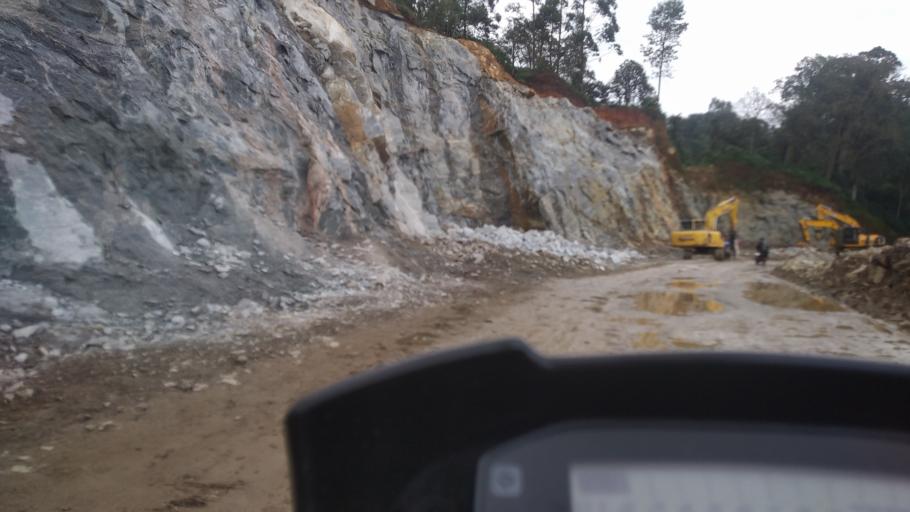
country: IN
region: Kerala
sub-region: Idukki
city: Munnar
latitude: 10.0352
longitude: 77.1430
